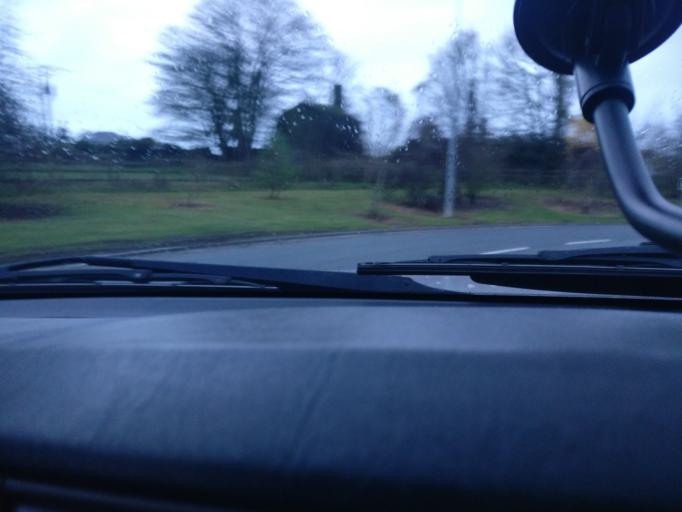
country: IE
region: Connaught
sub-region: County Galway
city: Ballinasloe
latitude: 53.3162
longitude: -8.2451
